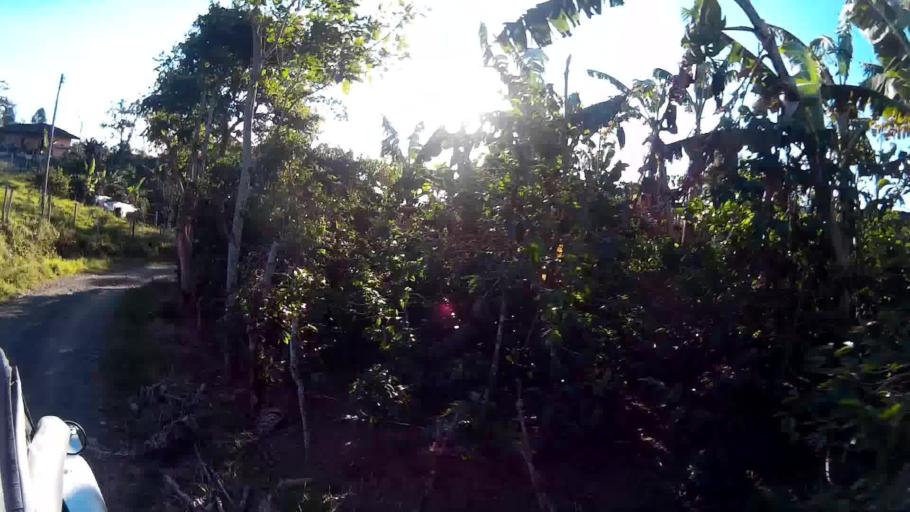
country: CO
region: Quindio
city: Filandia
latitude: 4.7249
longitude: -75.6817
